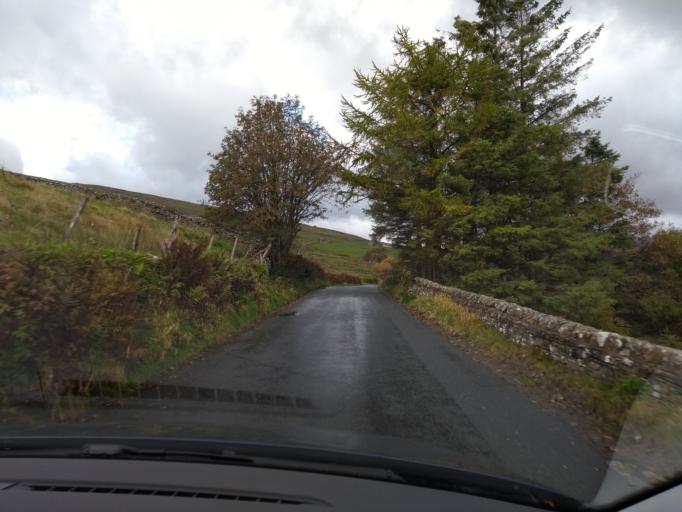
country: GB
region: England
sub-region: Cumbria
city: Kirkby Stephen
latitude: 54.3850
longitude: -2.1732
